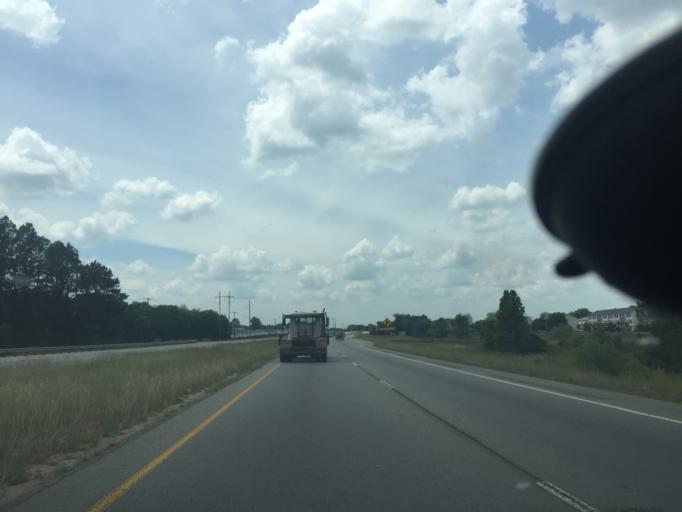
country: US
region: Georgia
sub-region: Bulloch County
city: Statesboro
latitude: 32.4059
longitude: -81.7723
